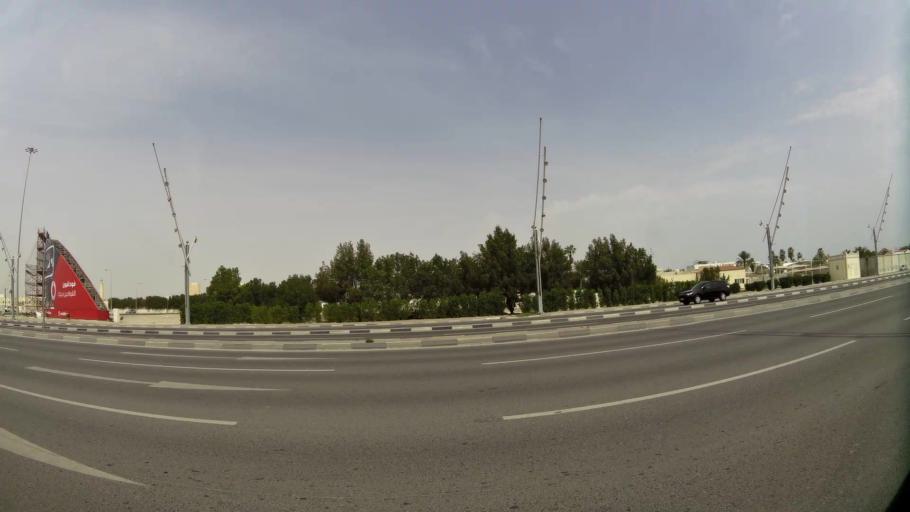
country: QA
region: Baladiyat ad Dawhah
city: Doha
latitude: 25.2683
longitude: 51.4787
